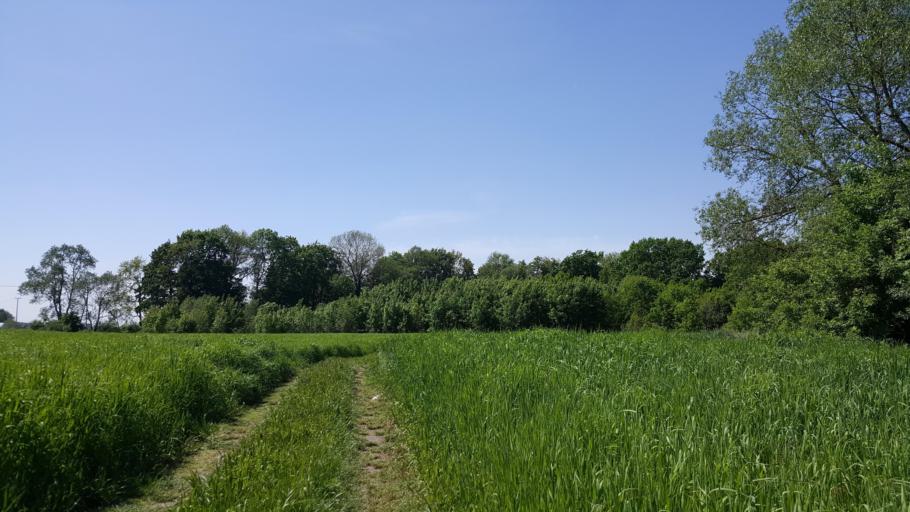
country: BY
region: Brest
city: Charnawchytsy
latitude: 52.2692
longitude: 23.7579
